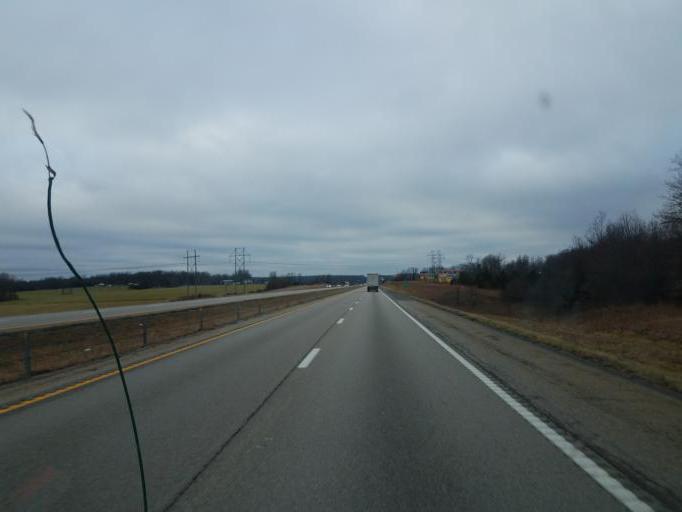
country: US
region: Missouri
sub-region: Laclede County
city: Lebanon
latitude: 37.5831
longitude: -92.7458
